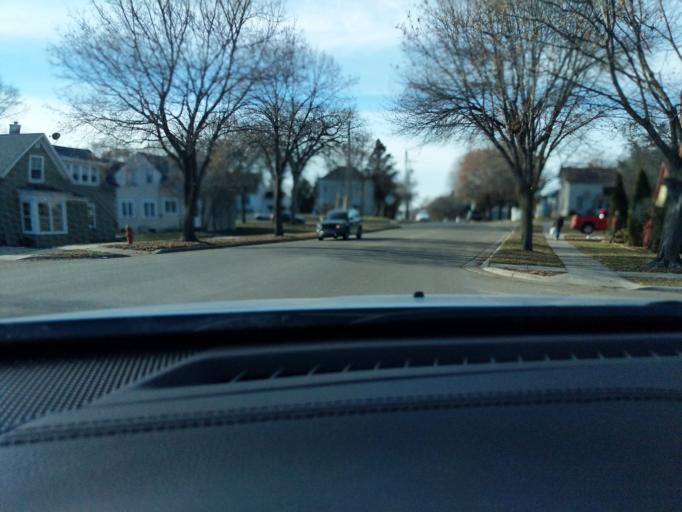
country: US
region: Minnesota
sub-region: Yellow Medicine County
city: Granite Falls
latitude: 44.8069
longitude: -95.5434
